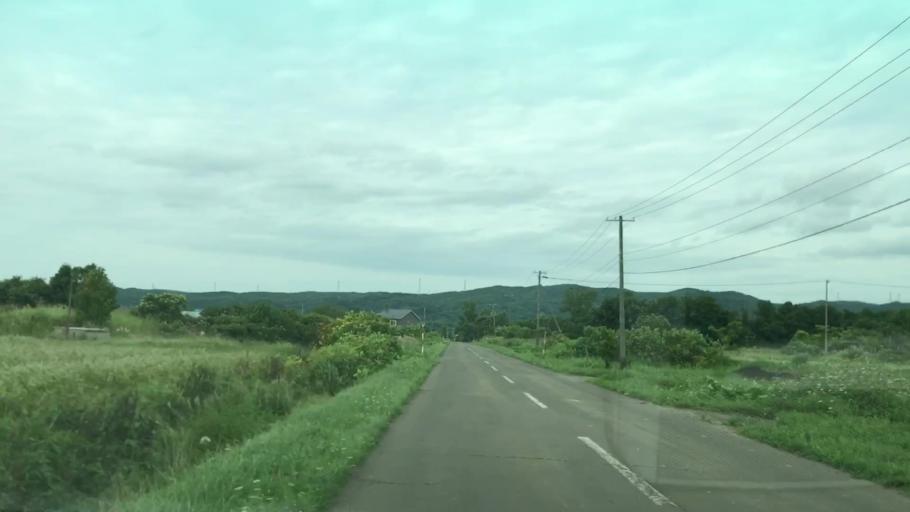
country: JP
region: Hokkaido
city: Iwanai
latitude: 43.0319
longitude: 140.5689
